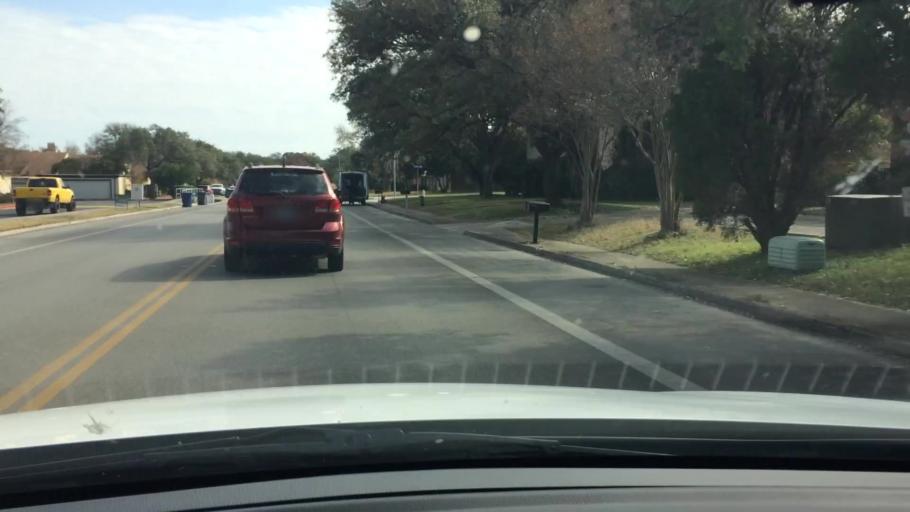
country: US
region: Texas
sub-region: Bexar County
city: Hollywood Park
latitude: 29.5784
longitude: -98.4736
